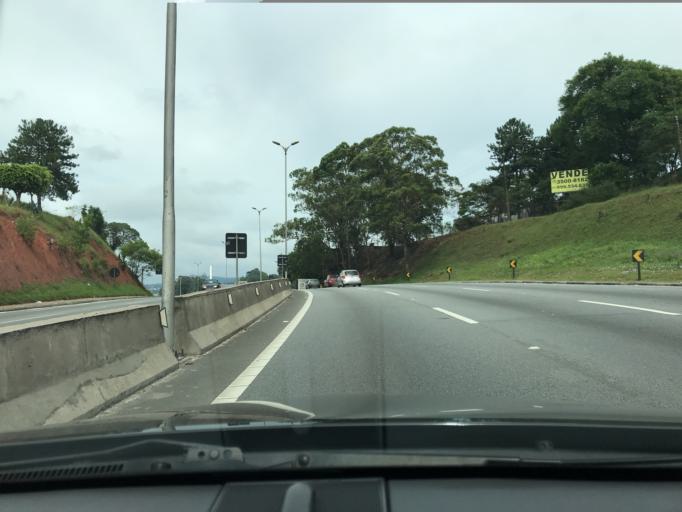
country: BR
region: Sao Paulo
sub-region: Cotia
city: Cotia
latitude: -23.5988
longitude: -46.8900
